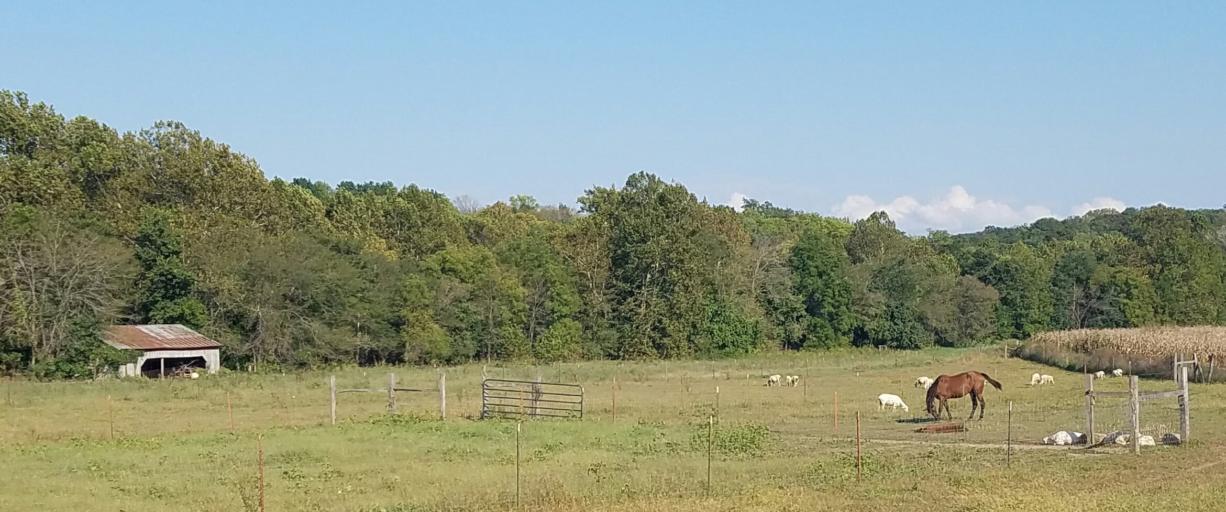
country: US
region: Missouri
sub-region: Moniteau County
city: California
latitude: 38.7428
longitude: -92.6267
